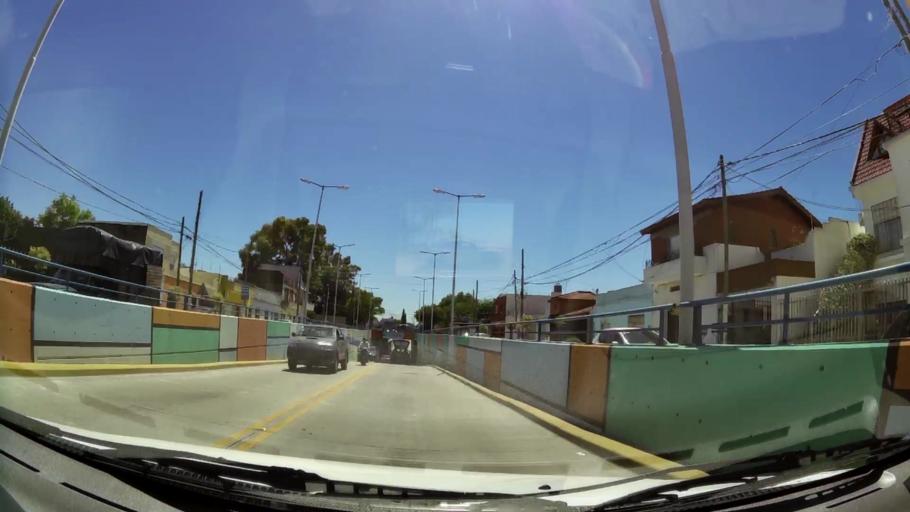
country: AR
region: Buenos Aires
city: Caseros
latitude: -34.5918
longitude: -58.5657
